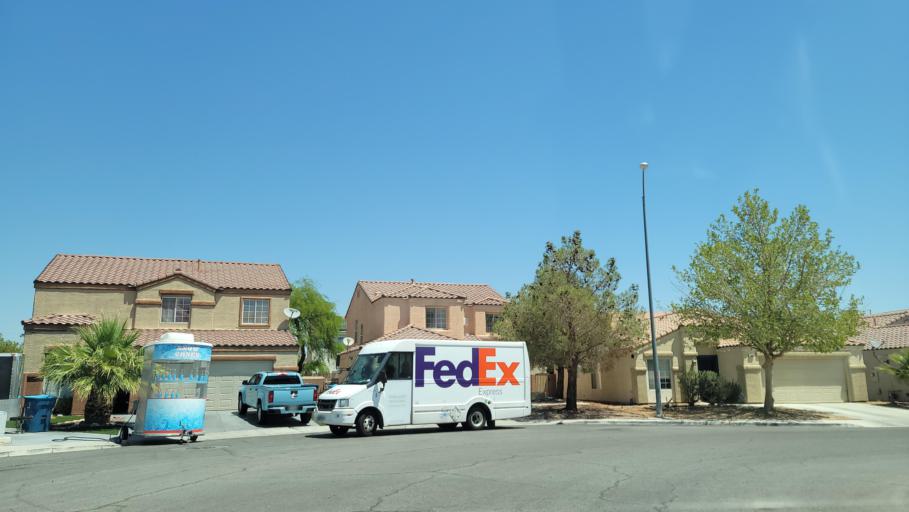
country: US
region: Nevada
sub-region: Clark County
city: Spring Valley
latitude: 36.0829
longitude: -115.2573
